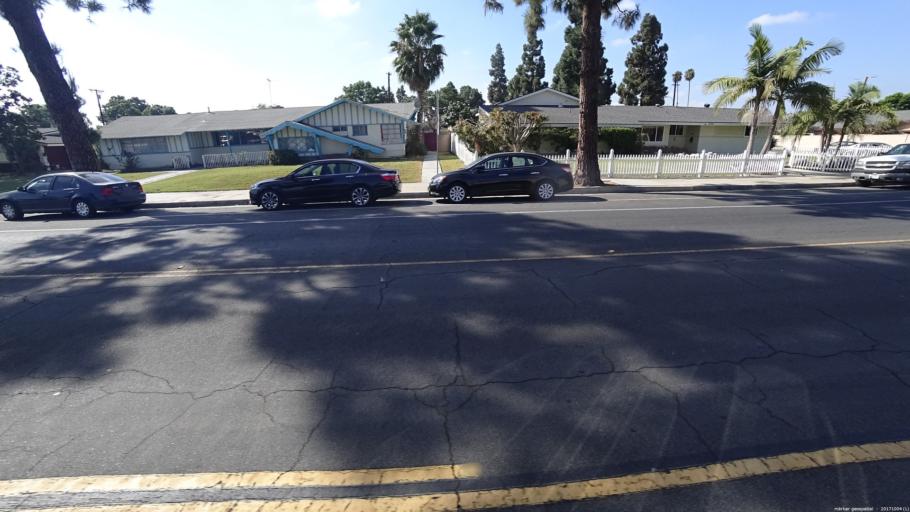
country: US
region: California
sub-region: Orange County
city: Garden Grove
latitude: 33.7962
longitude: -117.9490
